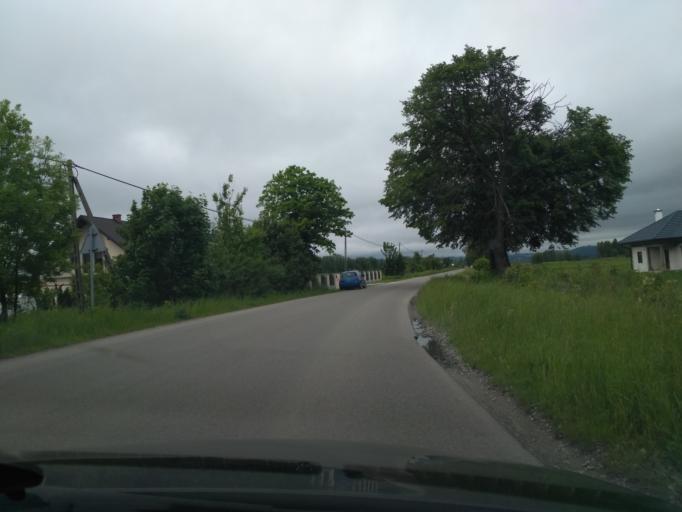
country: PL
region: Subcarpathian Voivodeship
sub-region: Powiat jasielski
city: Brzyska
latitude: 49.8237
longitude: 21.3938
